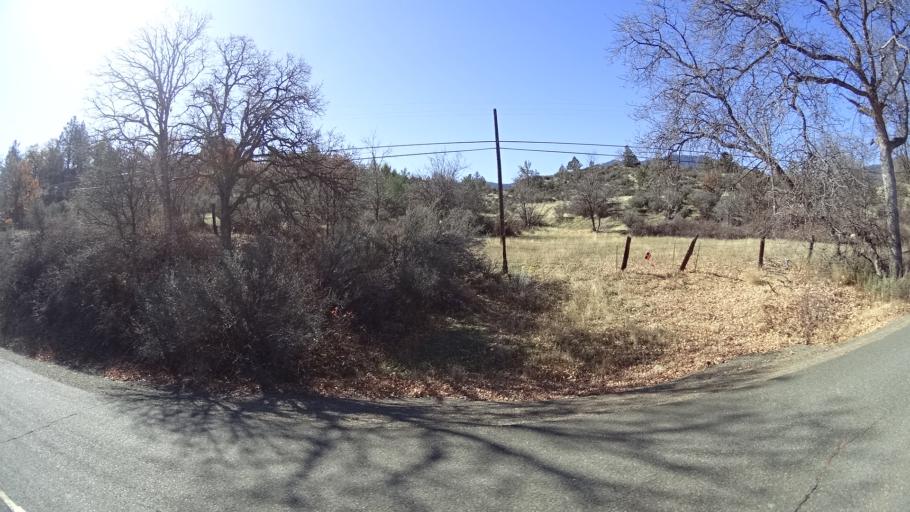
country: US
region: California
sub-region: Siskiyou County
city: Montague
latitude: 41.9175
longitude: -122.5655
